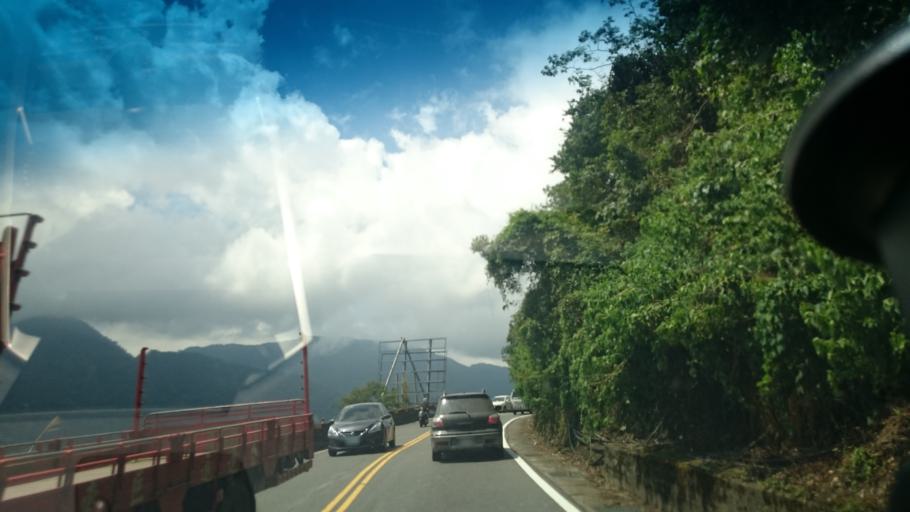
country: TW
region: Taiwan
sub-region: Nantou
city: Puli
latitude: 24.0369
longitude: 121.1444
